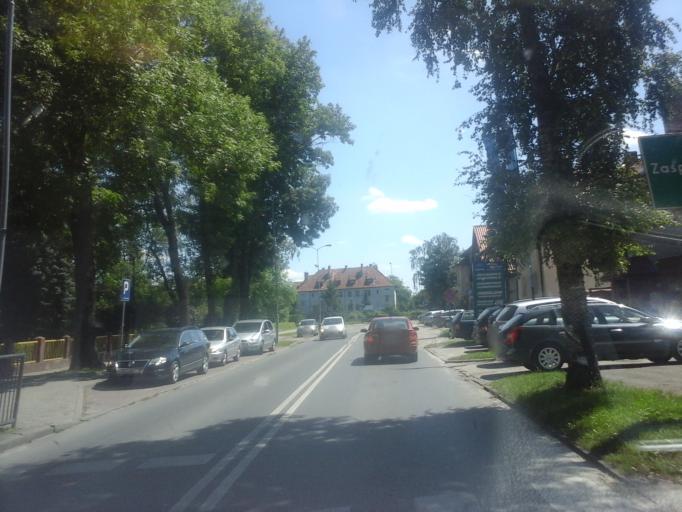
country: PL
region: West Pomeranian Voivodeship
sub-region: Powiat bialogardzki
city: Bialogard
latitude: 54.0069
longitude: 15.9943
